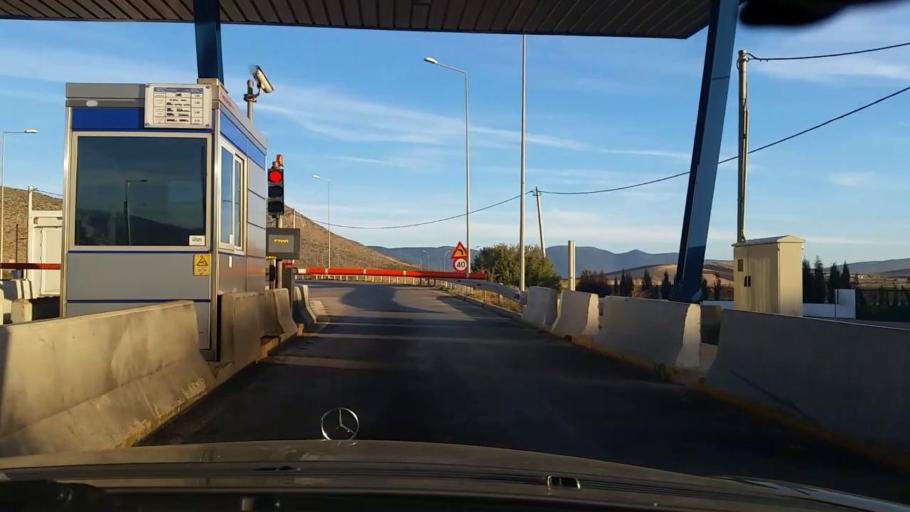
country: GR
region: Central Greece
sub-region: Nomos Voiotias
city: Thivai
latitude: 38.3662
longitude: 23.3247
